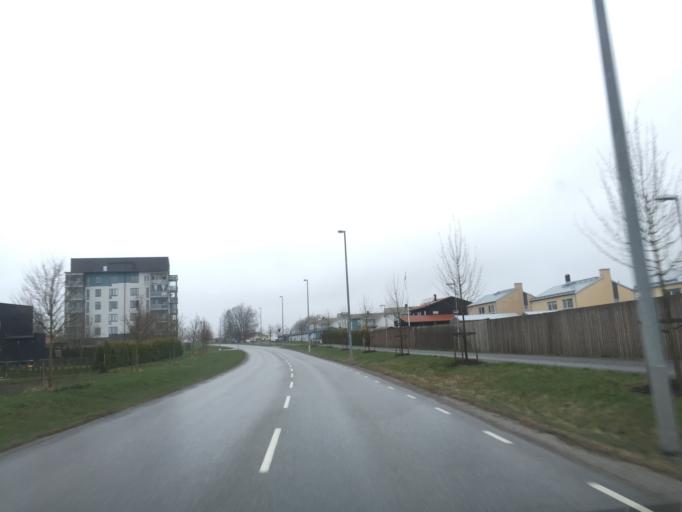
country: SE
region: OErebro
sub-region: Orebro Kommun
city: Orebro
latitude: 59.2659
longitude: 15.2584
